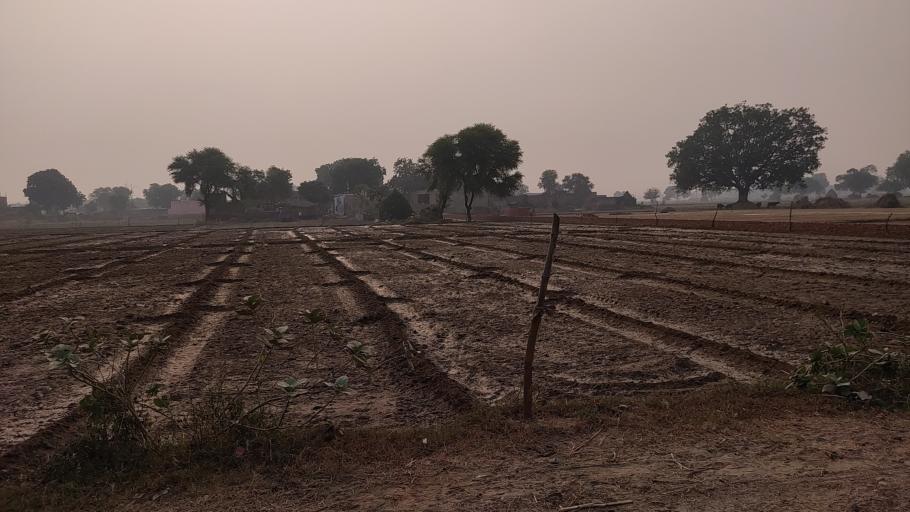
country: IN
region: Uttar Pradesh
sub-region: Mathura
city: Vrindavan
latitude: 27.5552
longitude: 77.7159
